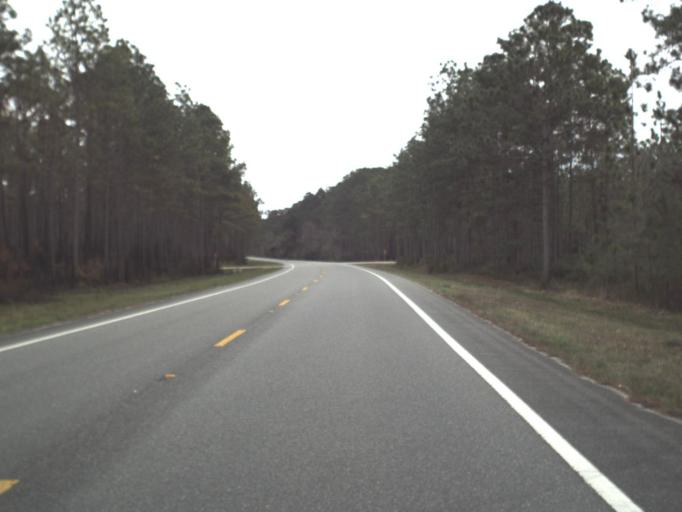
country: US
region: Florida
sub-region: Gadsden County
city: Midway
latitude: 30.3593
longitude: -84.5316
